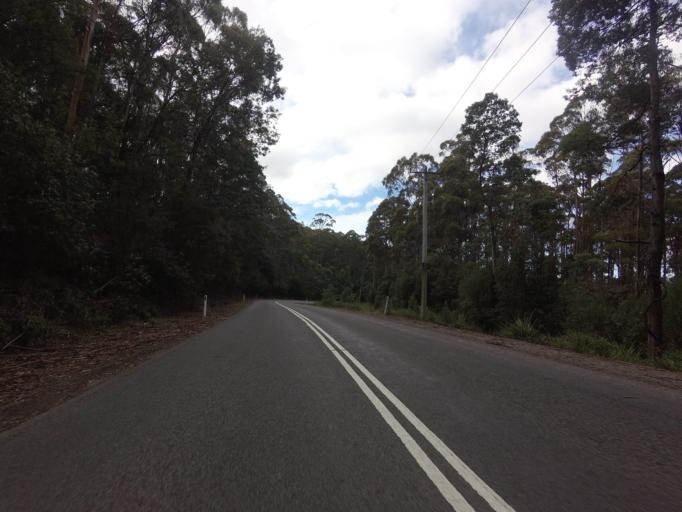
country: AU
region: Tasmania
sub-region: Clarence
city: Sandford
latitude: -43.1399
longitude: 147.8252
